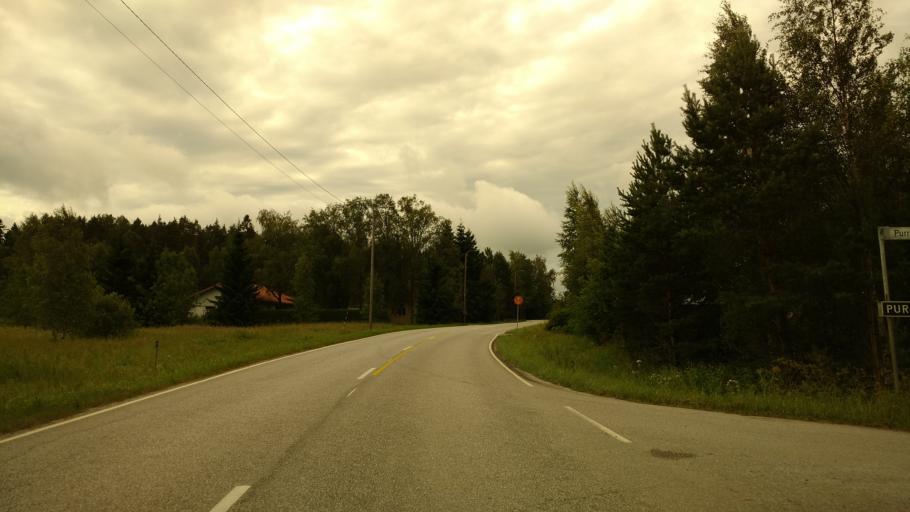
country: FI
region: Varsinais-Suomi
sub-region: Salo
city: Kuusjoki
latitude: 60.4837
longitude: 23.1627
